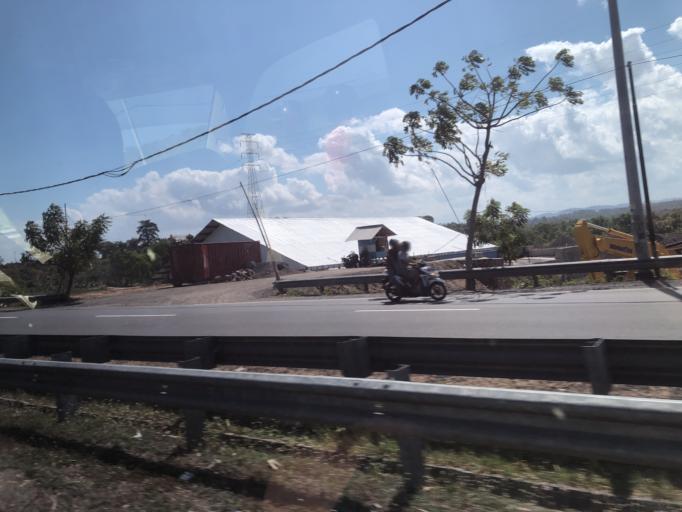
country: ID
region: Bali
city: Dawan
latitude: -8.5580
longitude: 115.4282
